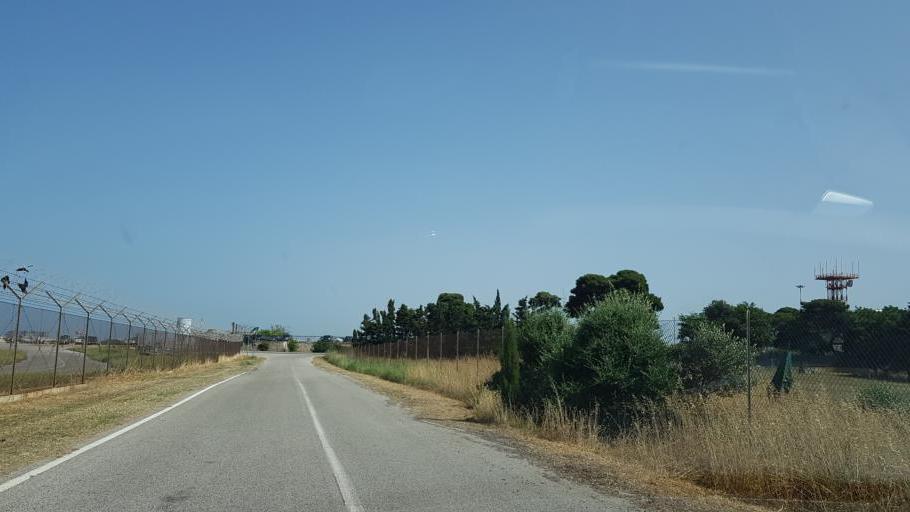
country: IT
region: Apulia
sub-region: Provincia di Brindisi
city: Materdomini
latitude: 40.6611
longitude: 17.9407
